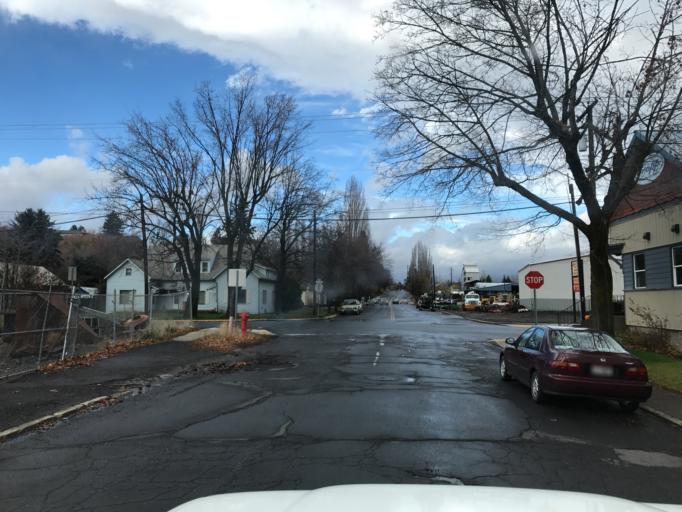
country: US
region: Idaho
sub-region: Latah County
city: Moscow
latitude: 46.7343
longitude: -117.0041
